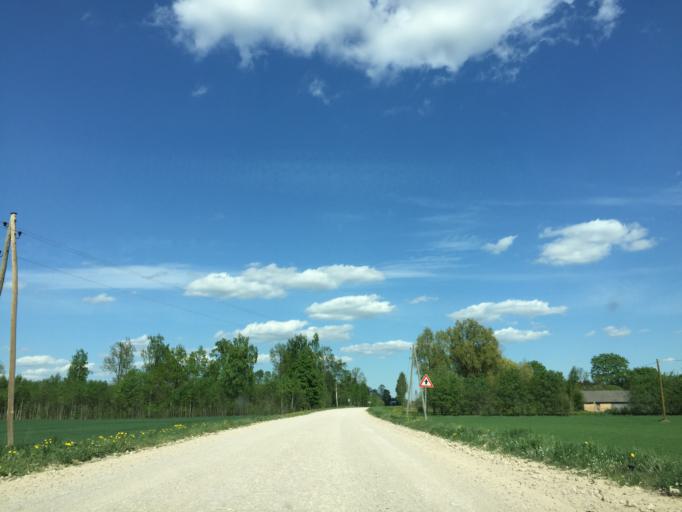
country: LV
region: Bauskas Rajons
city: Bauska
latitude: 56.3907
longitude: 24.0959
